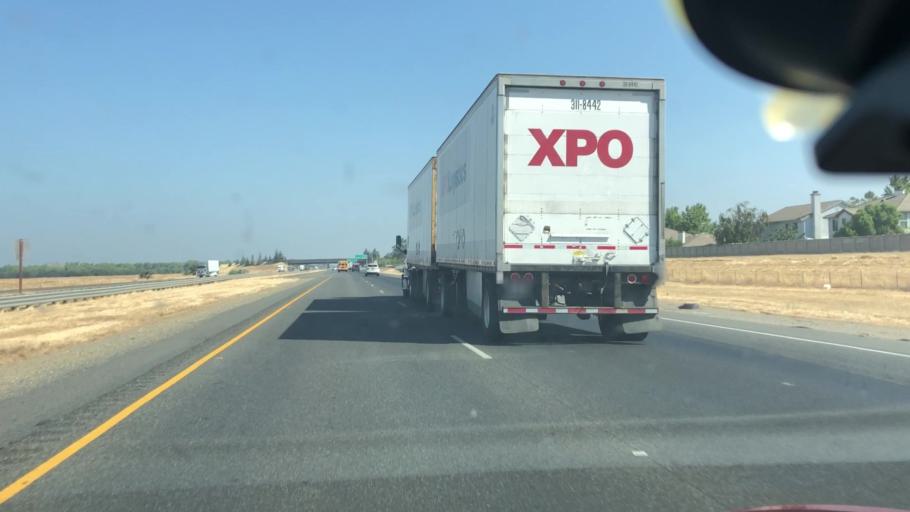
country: US
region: California
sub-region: Sacramento County
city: Laguna
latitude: 38.4191
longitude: -121.4857
